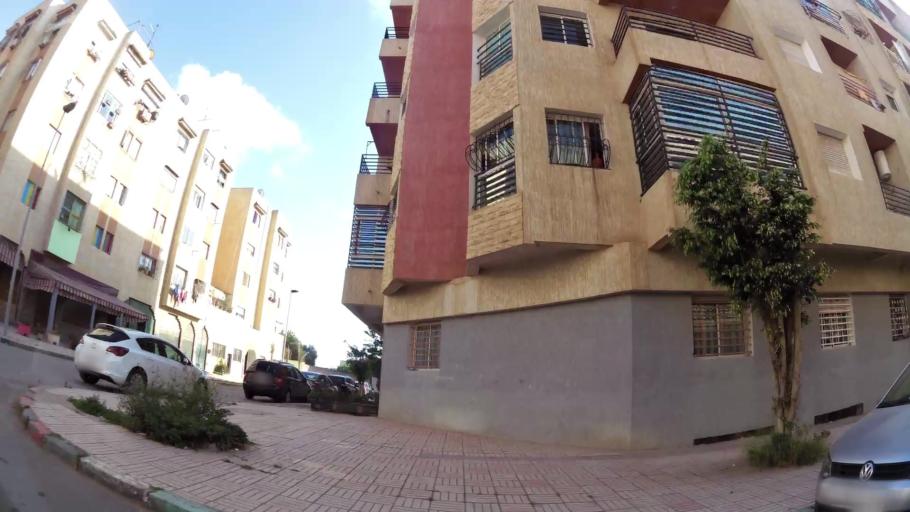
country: MA
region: Rabat-Sale-Zemmour-Zaer
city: Sale
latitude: 34.0506
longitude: -6.8015
